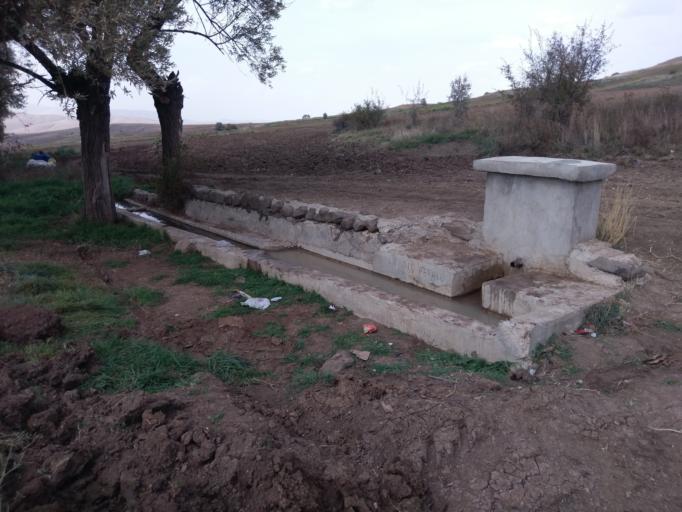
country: TR
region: Kayseri
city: Toklar
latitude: 38.4334
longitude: 36.0271
